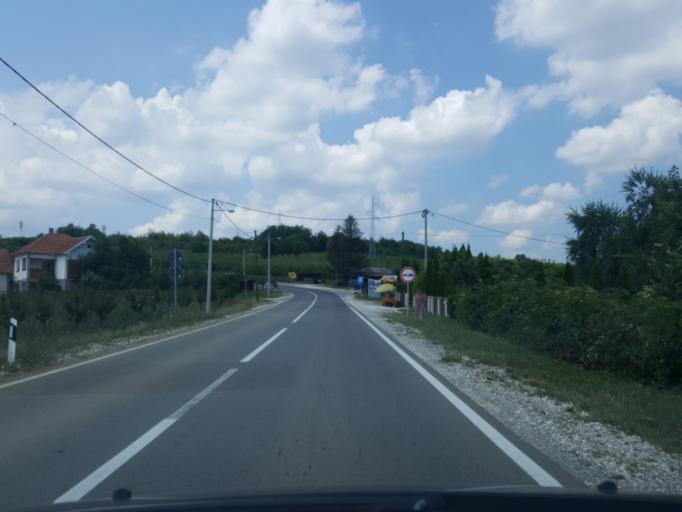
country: RS
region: Central Serbia
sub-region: Sumadijski Okrug
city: Topola
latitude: 44.2275
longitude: 20.6342
